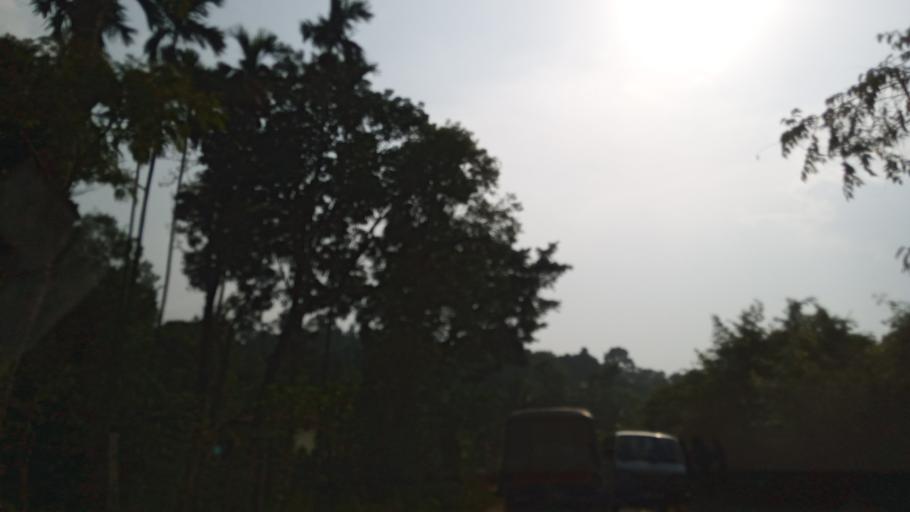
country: IN
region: Karnataka
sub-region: Chikmagalur
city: Mudigere
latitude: 13.0589
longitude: 75.6663
